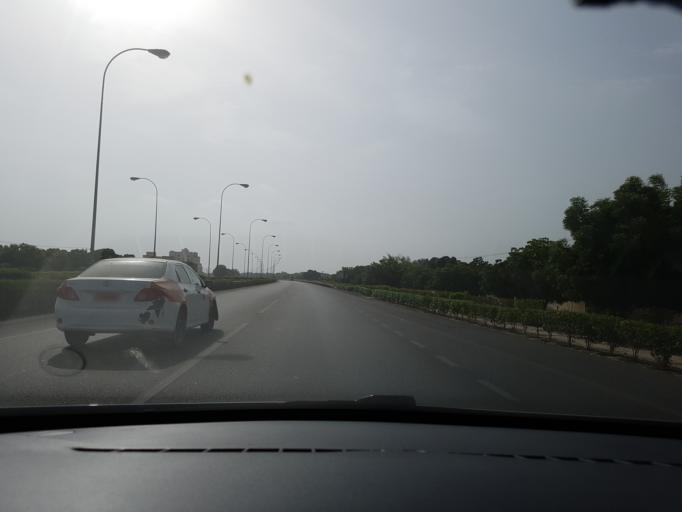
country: OM
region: Al Batinah
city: Al Sohar
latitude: 24.3975
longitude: 56.6699
